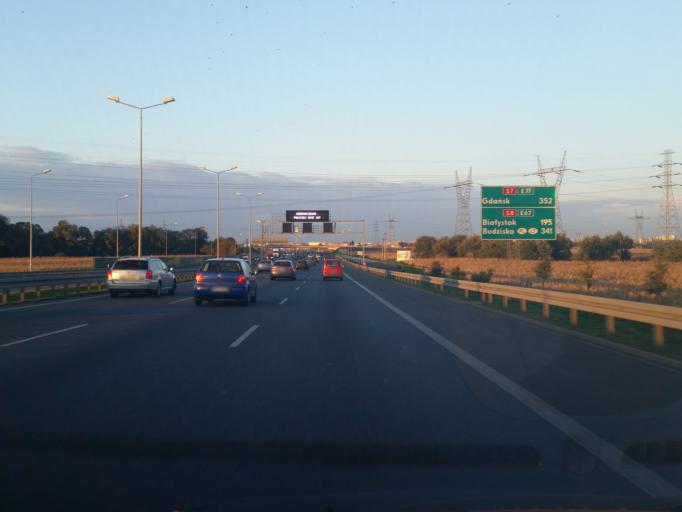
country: PL
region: Masovian Voivodeship
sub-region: Warszawa
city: Ursus
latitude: 52.2182
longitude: 20.8661
